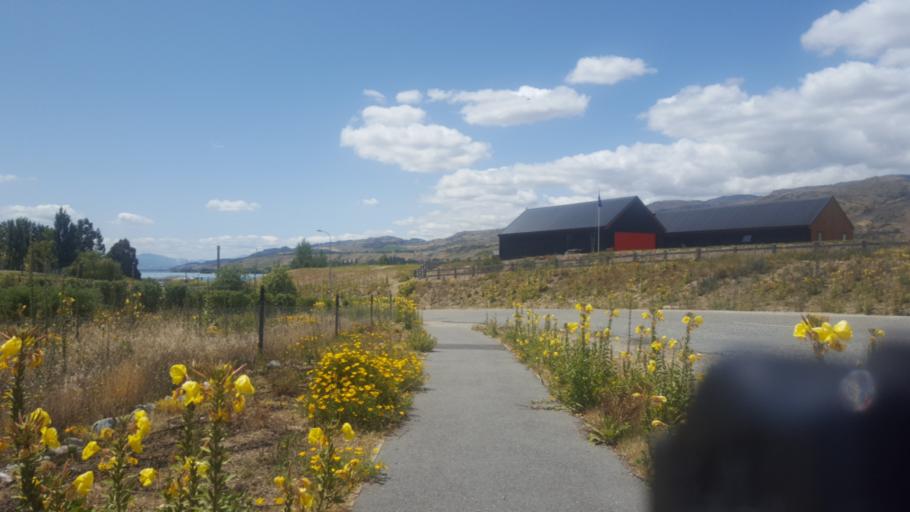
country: NZ
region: Otago
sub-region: Queenstown-Lakes District
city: Wanaka
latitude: -45.0298
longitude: 169.2056
